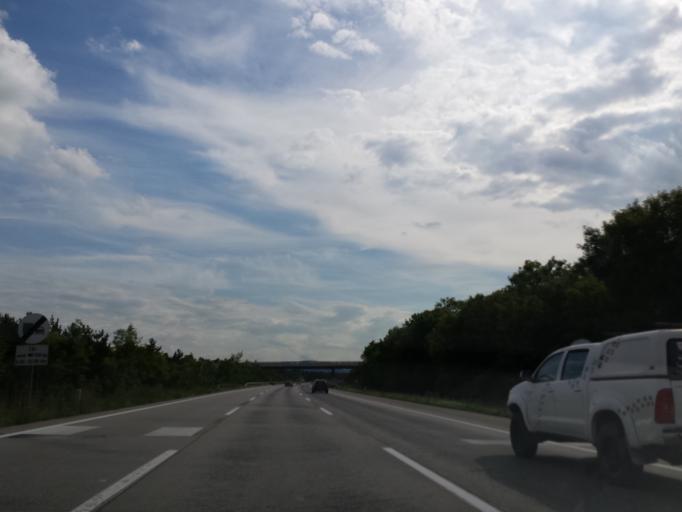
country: AT
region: Lower Austria
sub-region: Politischer Bezirk Wiener Neustadt
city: Bad Erlach
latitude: 47.7663
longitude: 16.2035
